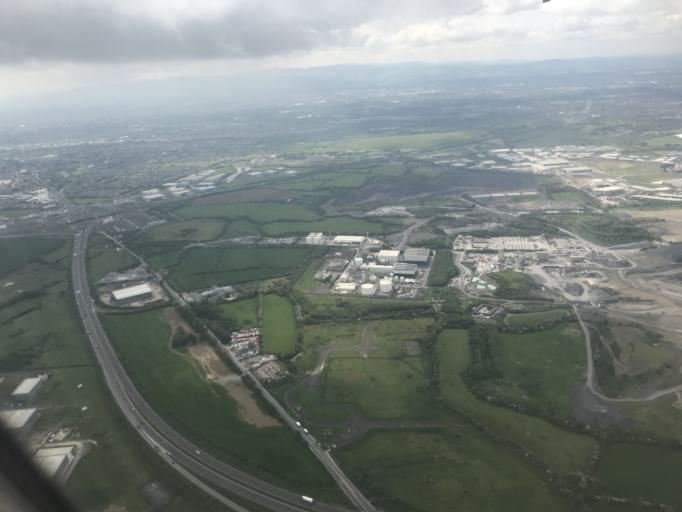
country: IE
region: Leinster
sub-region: Dublin City
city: Finglas
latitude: 53.4243
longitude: -6.3224
